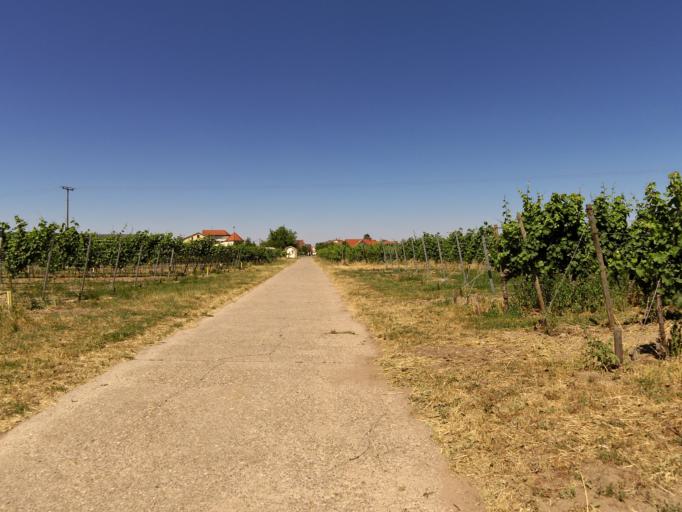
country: DE
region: Rheinland-Pfalz
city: Neustadt
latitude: 49.3619
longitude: 8.1704
